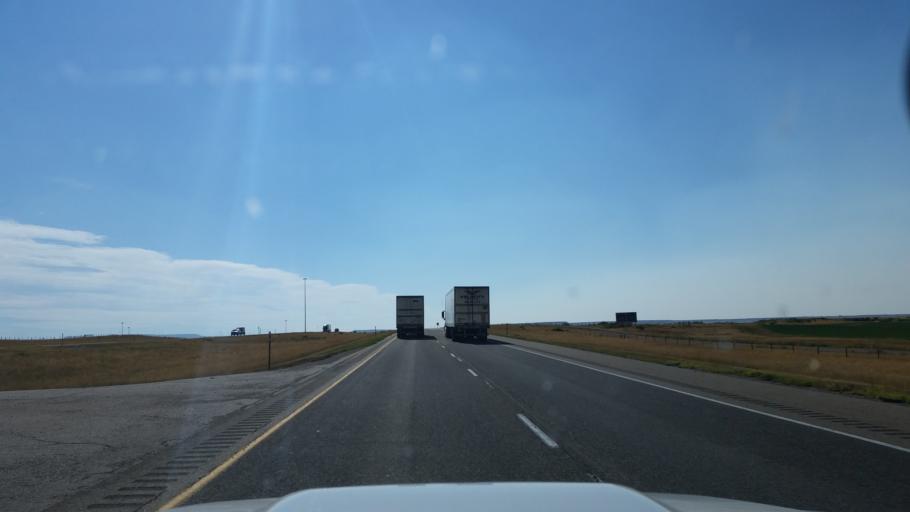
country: US
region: Wyoming
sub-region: Uinta County
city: Lyman
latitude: 41.3688
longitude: -110.2887
